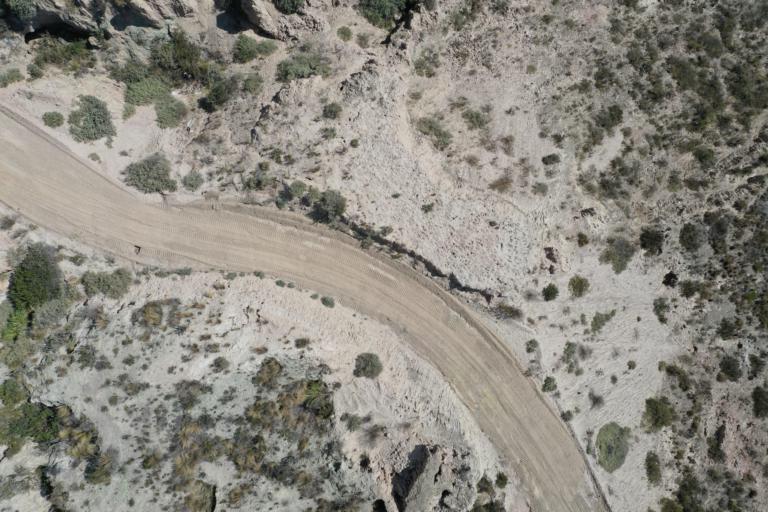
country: BO
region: La Paz
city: La Paz
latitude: -16.5605
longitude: -68.1302
